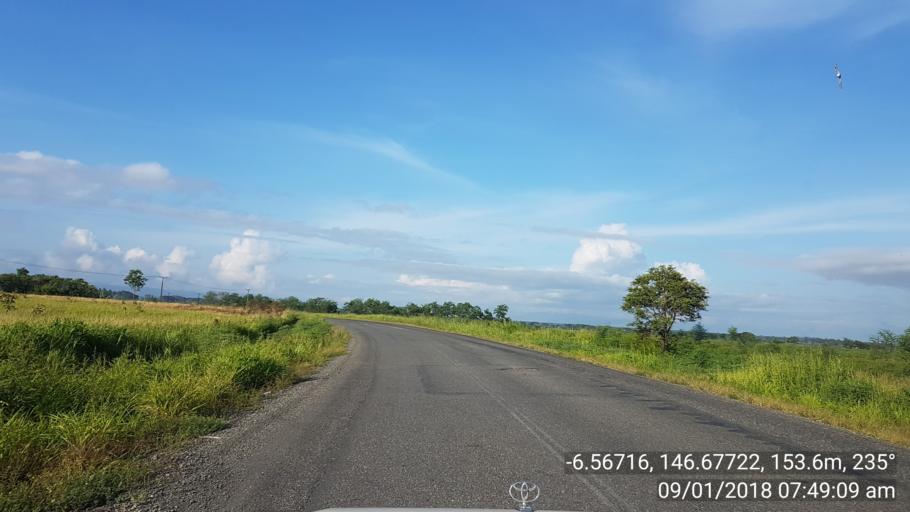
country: PG
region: Morobe
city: Lae
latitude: -6.5672
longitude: 146.6772
